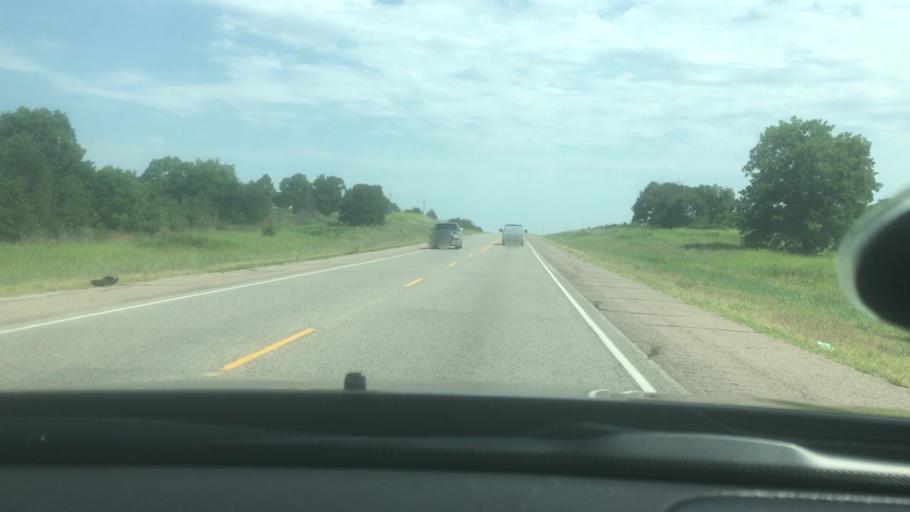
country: US
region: Oklahoma
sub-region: Seminole County
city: Maud
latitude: 35.0254
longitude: -96.9314
